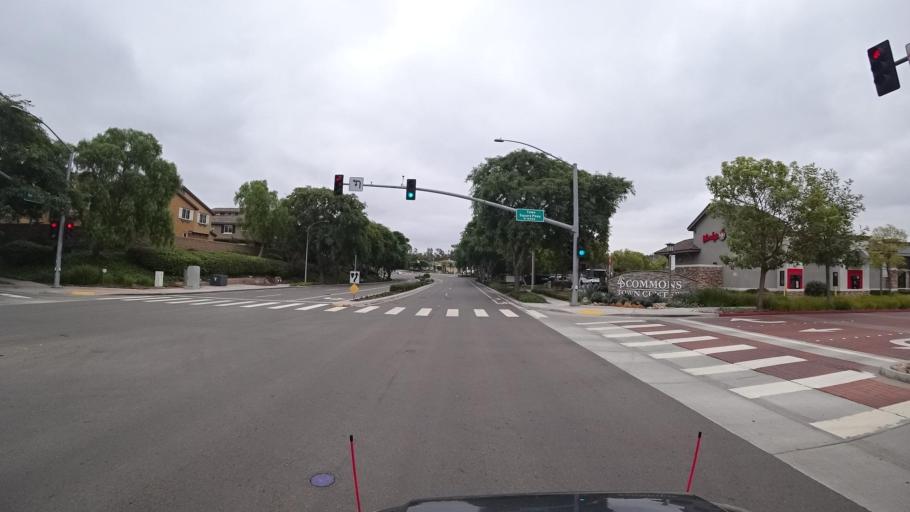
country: US
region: California
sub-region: San Diego County
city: Fairbanks Ranch
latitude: 33.0209
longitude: -117.1117
